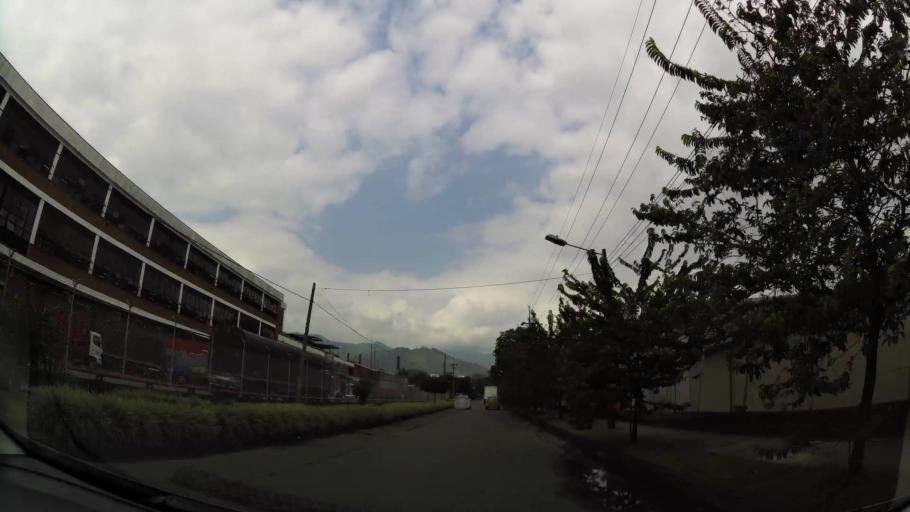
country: CO
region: Antioquia
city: Itagui
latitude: 6.2097
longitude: -75.5816
